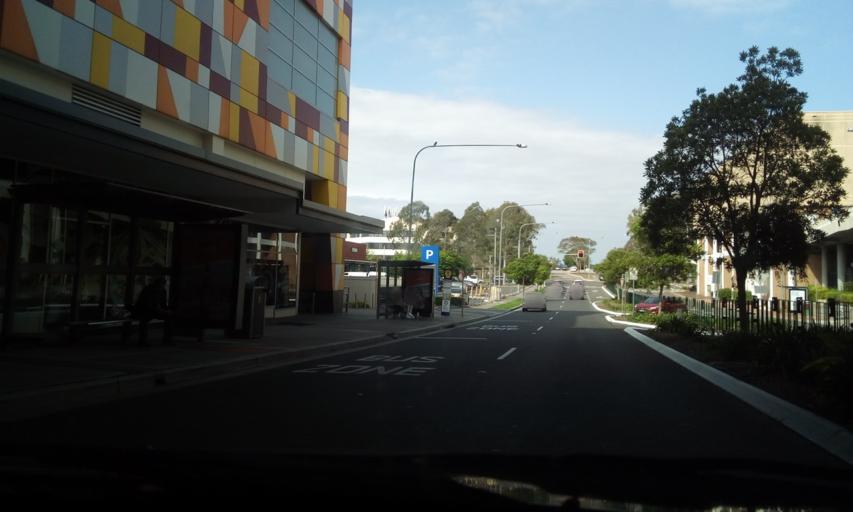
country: AU
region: New South Wales
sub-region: Campbelltown Municipality
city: Glen Alpine
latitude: -34.0741
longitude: 150.7972
